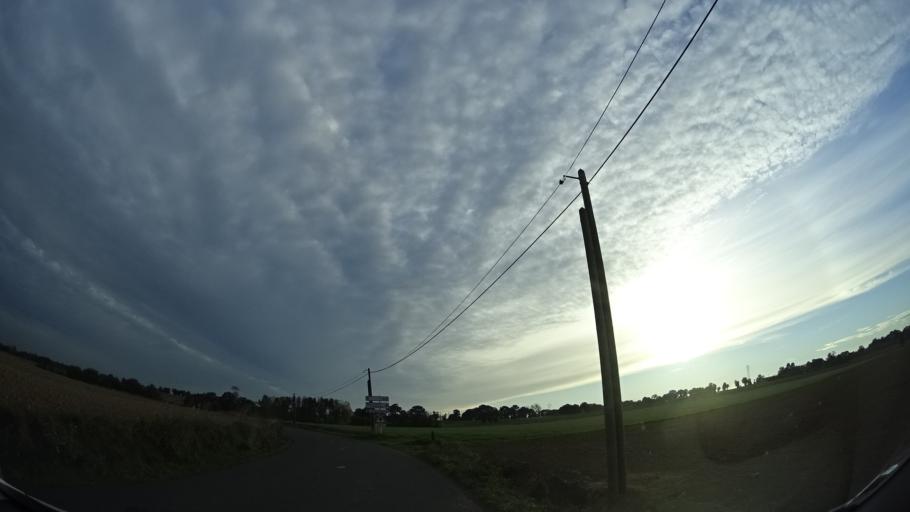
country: FR
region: Brittany
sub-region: Departement d'Ille-et-Vilaine
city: Geveze
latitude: 48.1906
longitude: -1.7938
